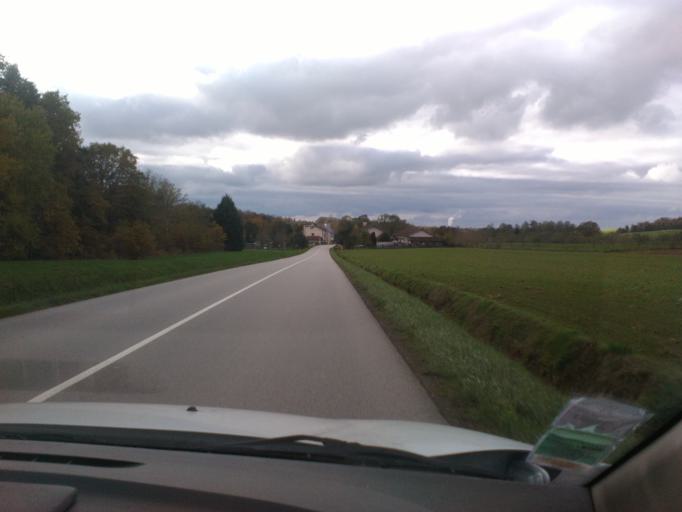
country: FR
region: Lorraine
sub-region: Departement des Vosges
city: Jeanmenil
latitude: 48.3541
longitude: 6.7204
